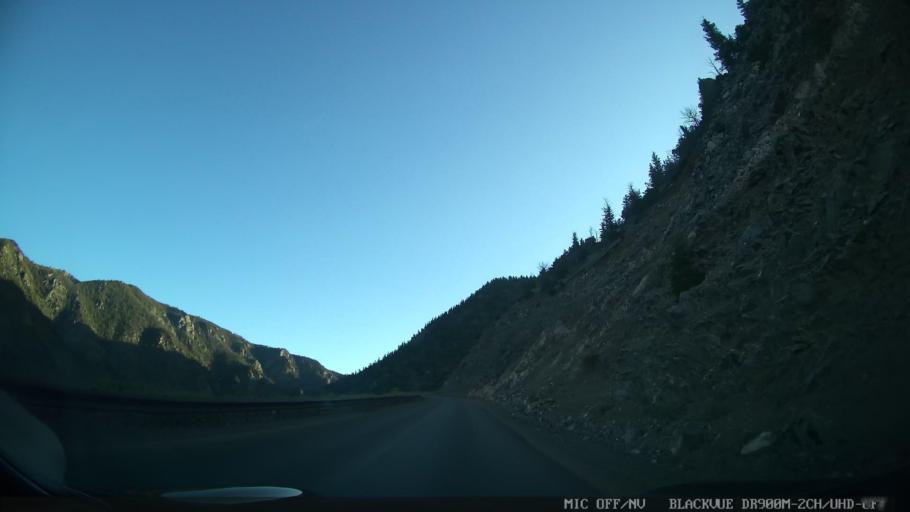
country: US
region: Colorado
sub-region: Grand County
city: Kremmling
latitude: 40.0003
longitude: -106.4866
